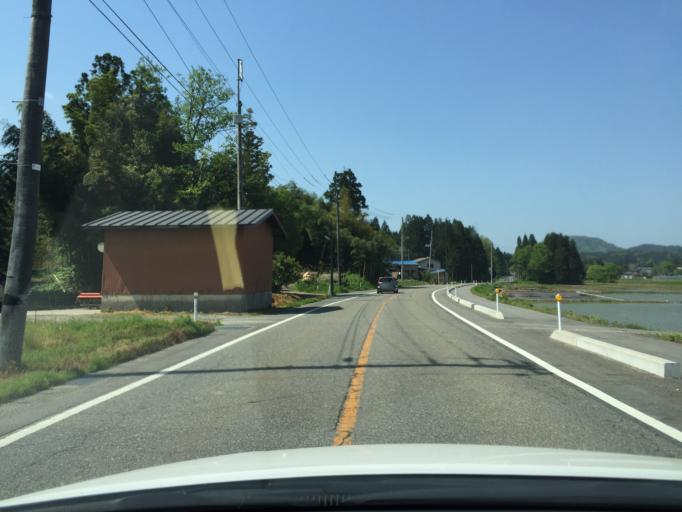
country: JP
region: Niigata
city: Muramatsu
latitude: 37.6699
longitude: 139.1457
